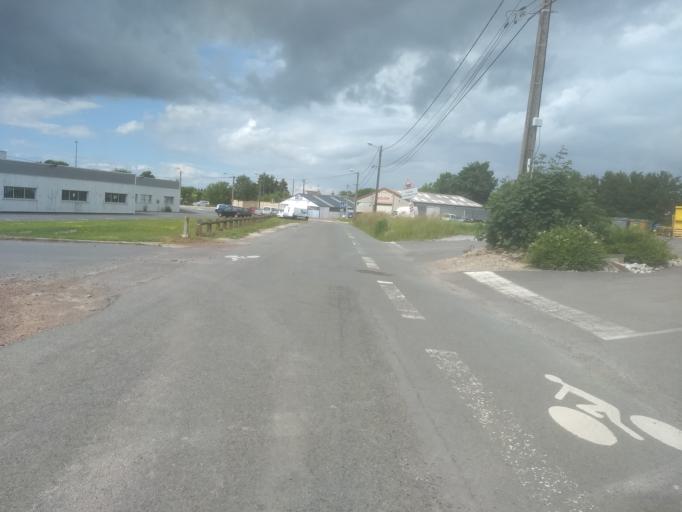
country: FR
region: Nord-Pas-de-Calais
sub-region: Departement du Pas-de-Calais
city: Dainville
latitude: 50.2729
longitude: 2.7209
